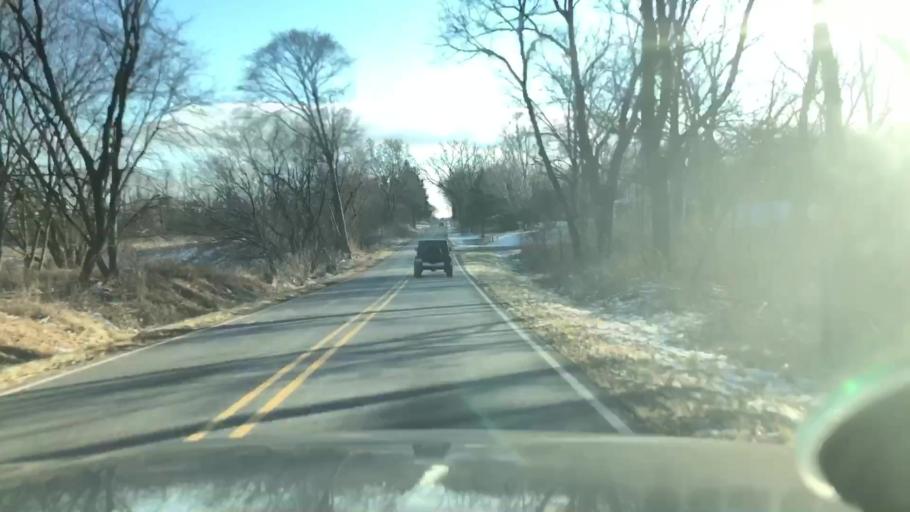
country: US
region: Michigan
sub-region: Jackson County
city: Vandercook Lake
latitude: 42.1246
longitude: -84.4515
